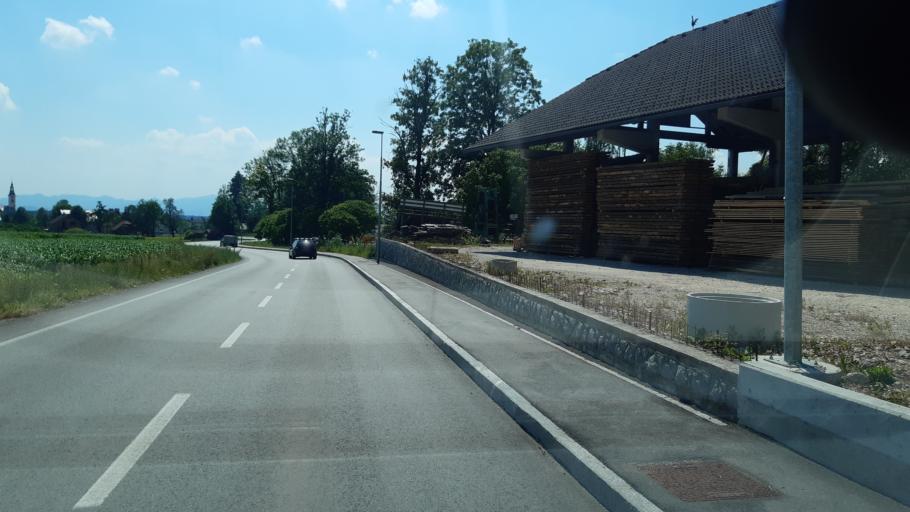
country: SI
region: Cerklje na Gorenjskem
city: Cerklje na Gorenjskem
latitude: 46.2600
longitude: 14.4914
